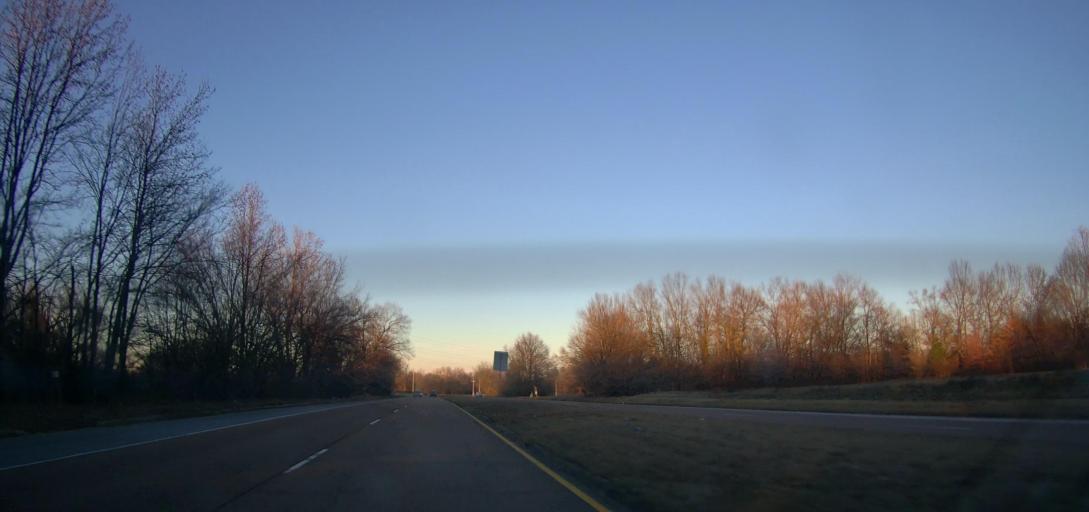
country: US
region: Tennessee
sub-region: Shelby County
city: Bartlett
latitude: 35.2500
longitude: -89.8955
